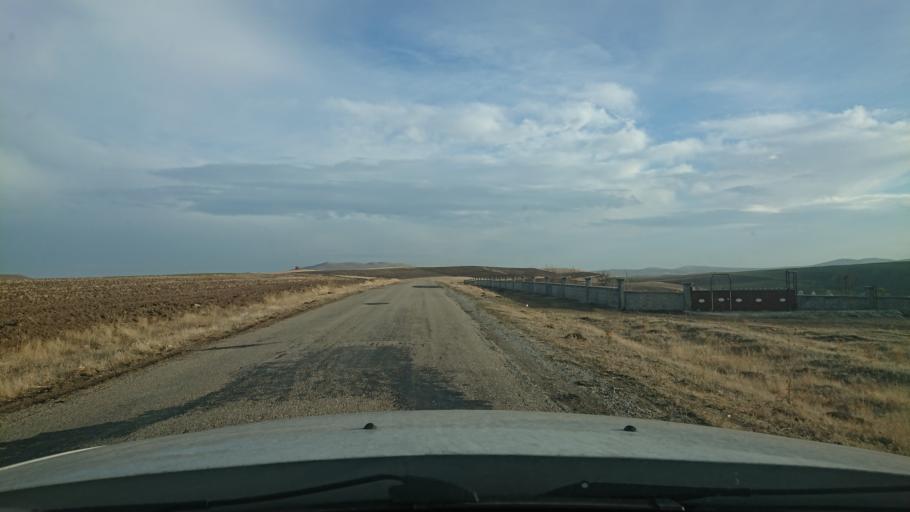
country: TR
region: Aksaray
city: Acipinar
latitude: 38.6625
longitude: 33.8446
